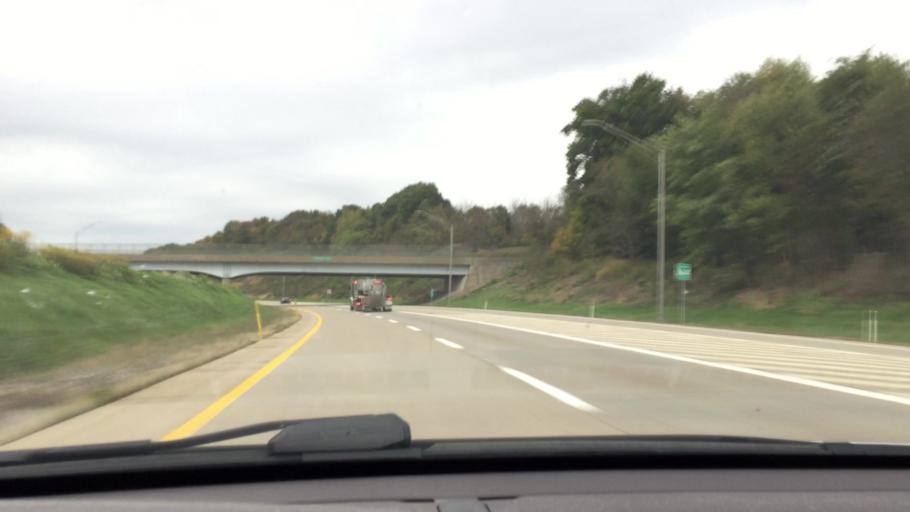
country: US
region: Pennsylvania
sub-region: Beaver County
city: Big Beaver
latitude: 40.8005
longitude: -80.3614
